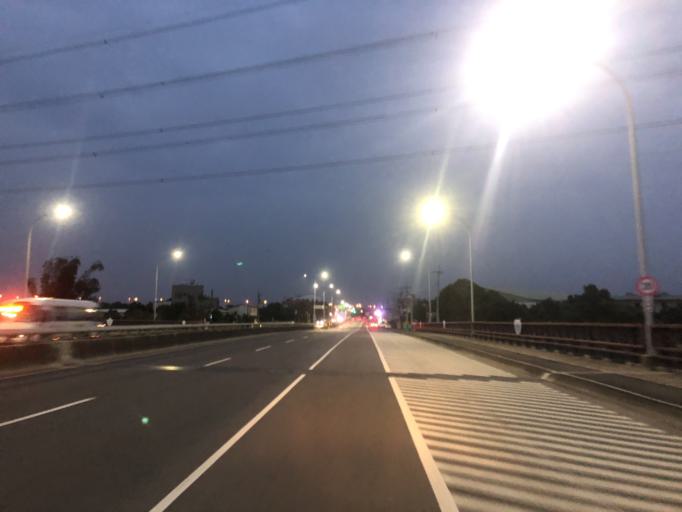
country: TW
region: Taiwan
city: Yujing
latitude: 23.1562
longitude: 120.3385
